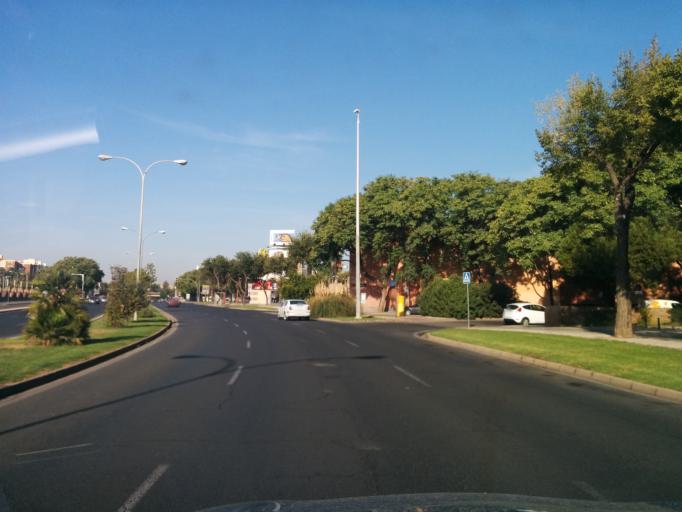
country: ES
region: Andalusia
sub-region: Provincia de Sevilla
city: Sevilla
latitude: 37.4058
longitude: -5.9317
